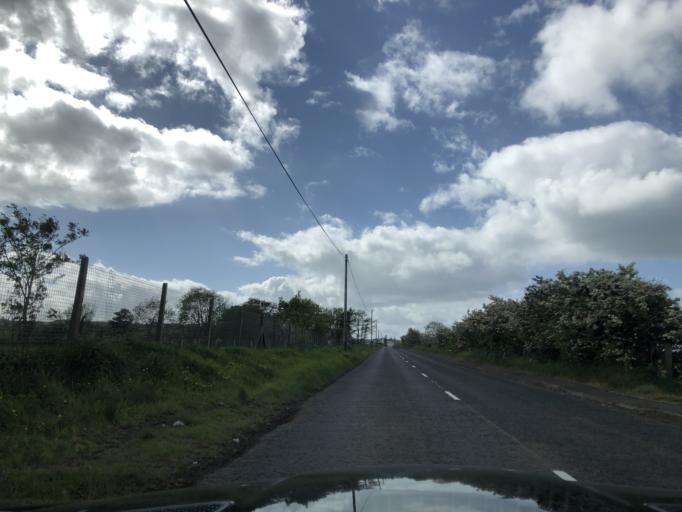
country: GB
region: Northern Ireland
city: Bushmills
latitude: 55.2066
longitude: -6.5336
